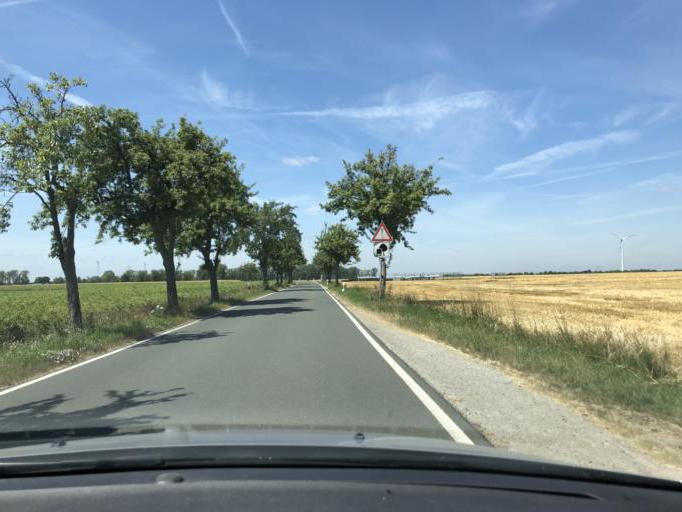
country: DE
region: Thuringia
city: Schkolen
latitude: 51.0593
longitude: 11.7960
